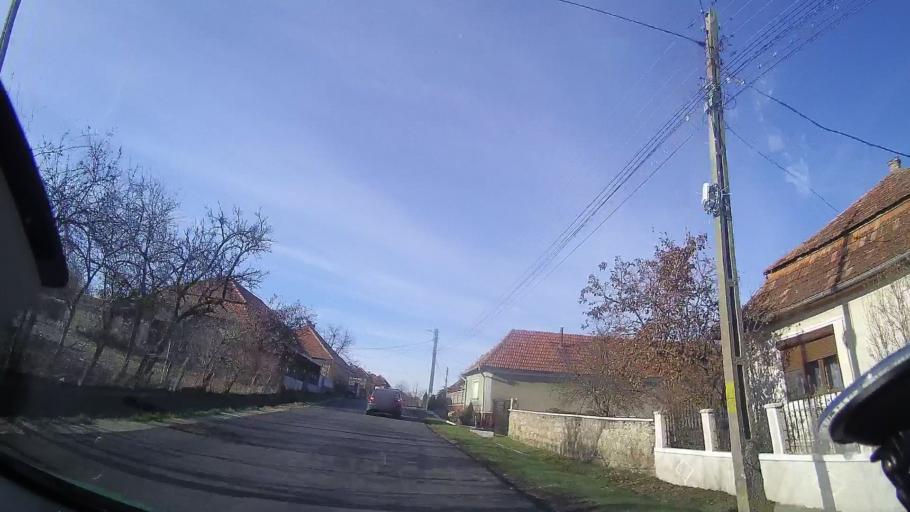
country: RO
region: Bihor
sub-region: Comuna Magesti
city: Magesti
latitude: 47.0152
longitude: 22.4373
